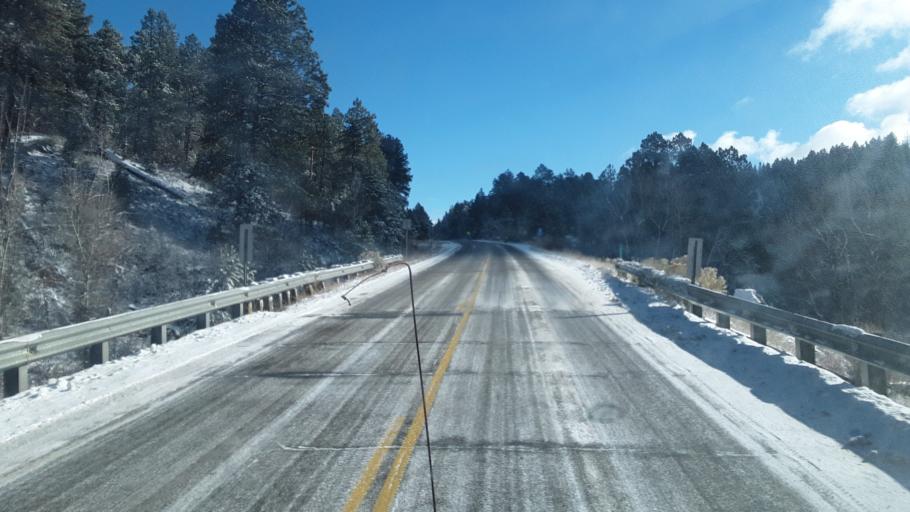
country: US
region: Colorado
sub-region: La Plata County
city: Durango
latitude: 37.3256
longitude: -107.7548
